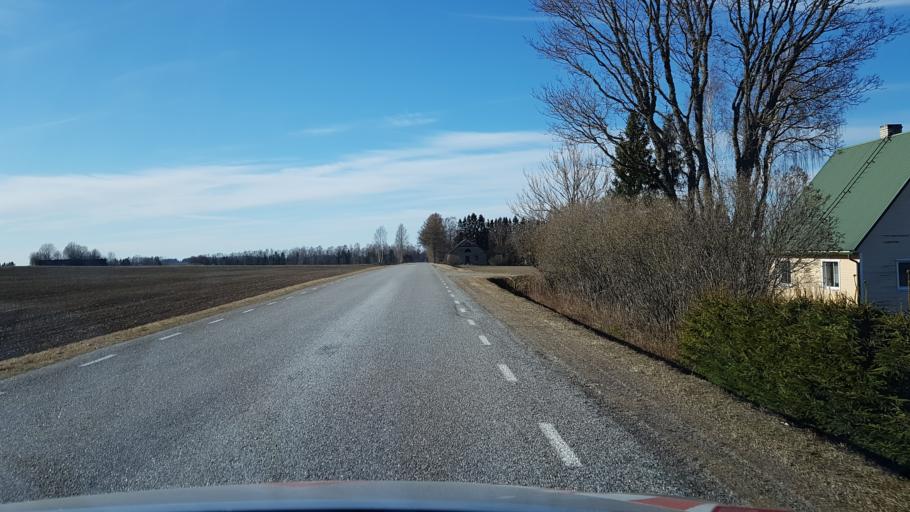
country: EE
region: Laeaene-Virumaa
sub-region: Kadrina vald
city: Kadrina
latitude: 59.3313
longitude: 26.1328
